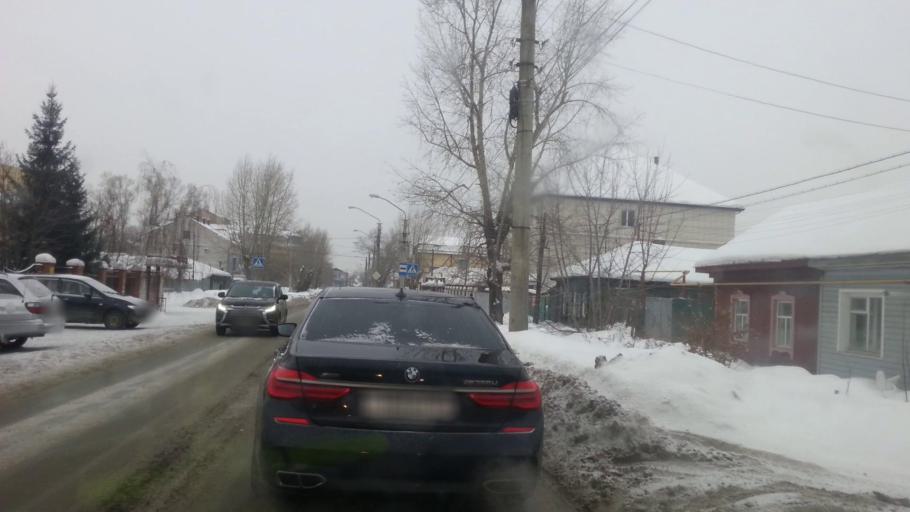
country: RU
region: Altai Krai
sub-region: Gorod Barnaulskiy
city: Barnaul
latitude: 53.3322
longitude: 83.7658
